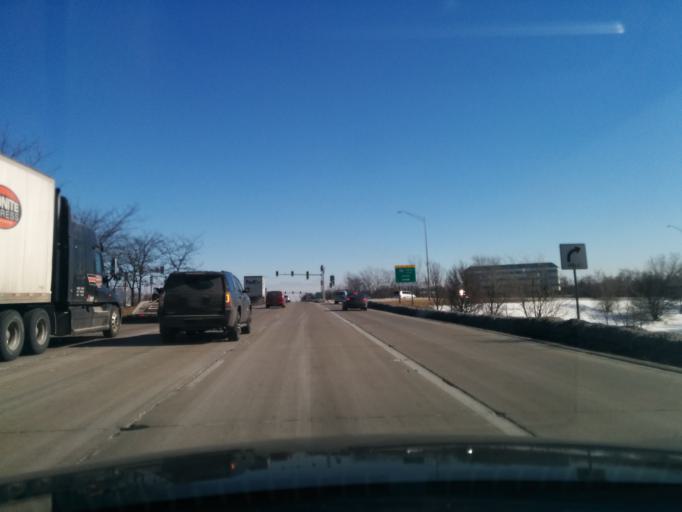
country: US
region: Illinois
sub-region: DuPage County
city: Glendale Heights
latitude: 41.9040
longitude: -88.0405
